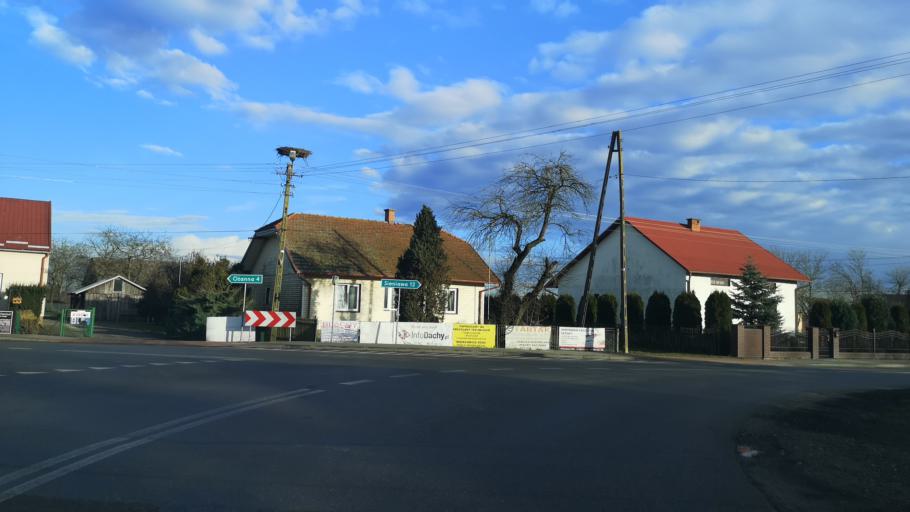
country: PL
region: Subcarpathian Voivodeship
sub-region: Powiat lezajski
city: Piskorowice
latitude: 50.2476
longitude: 22.5038
